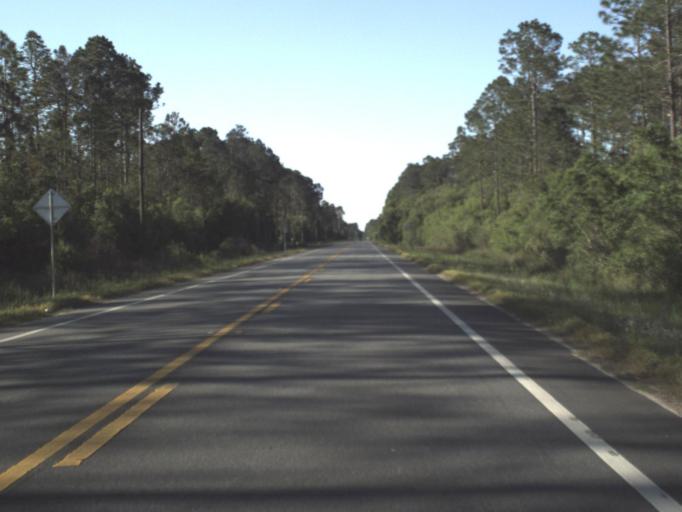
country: US
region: Florida
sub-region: Liberty County
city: Bristol
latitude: 30.3374
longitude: -84.8221
